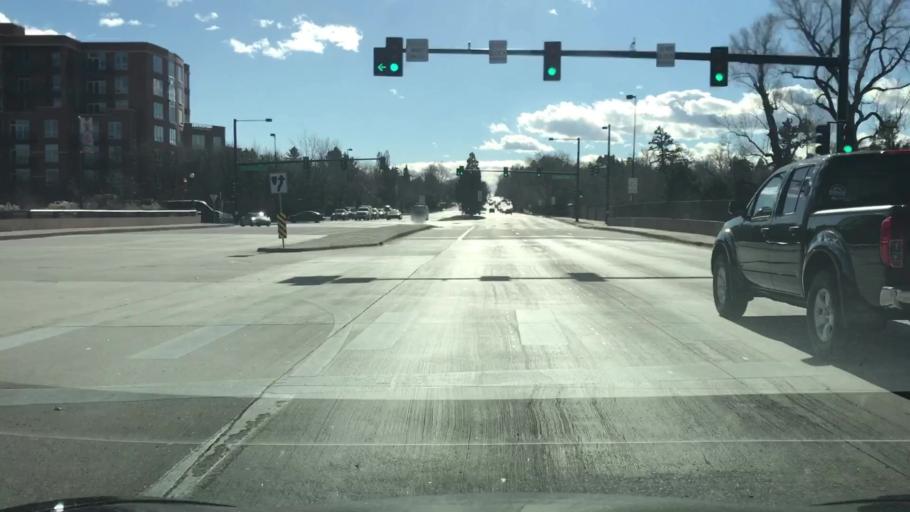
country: US
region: Colorado
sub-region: Arapahoe County
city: Glendale
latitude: 39.7163
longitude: -104.9593
